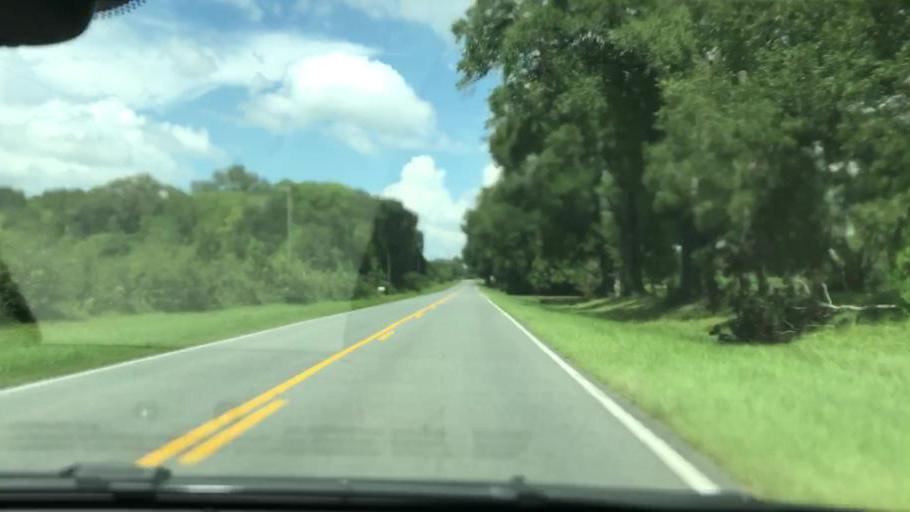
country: US
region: Florida
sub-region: Jackson County
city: Malone
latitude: 30.9130
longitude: -85.1191
